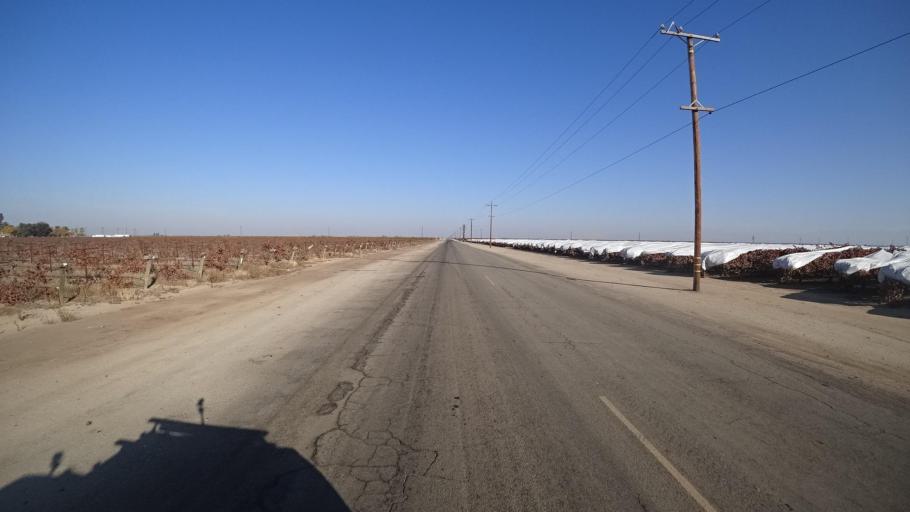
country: US
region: California
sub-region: Tulare County
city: Richgrove
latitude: 35.7441
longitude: -119.1696
